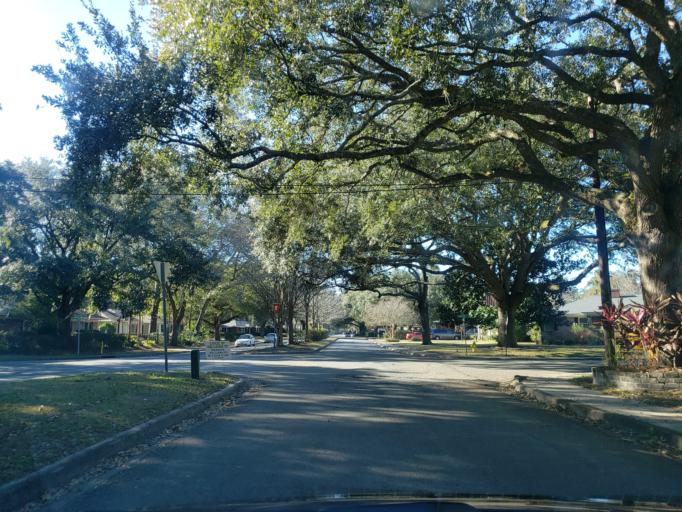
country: US
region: Georgia
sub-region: Chatham County
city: Thunderbolt
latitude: 32.0220
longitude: -81.0967
